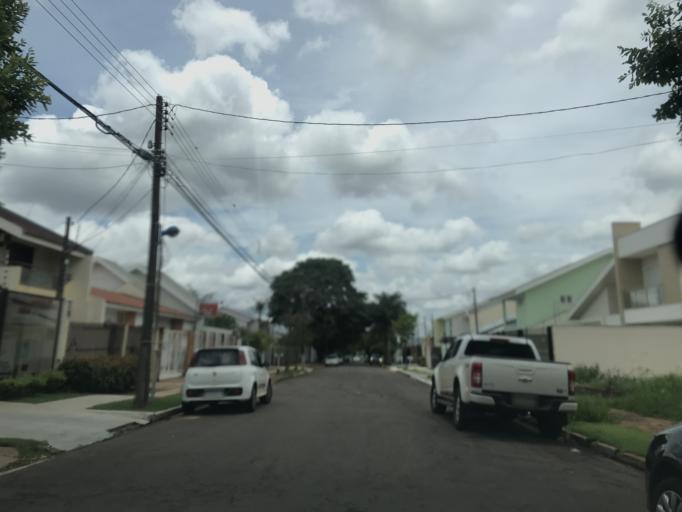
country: BR
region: Parana
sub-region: Maringa
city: Maringa
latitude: -23.4482
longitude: -51.9566
